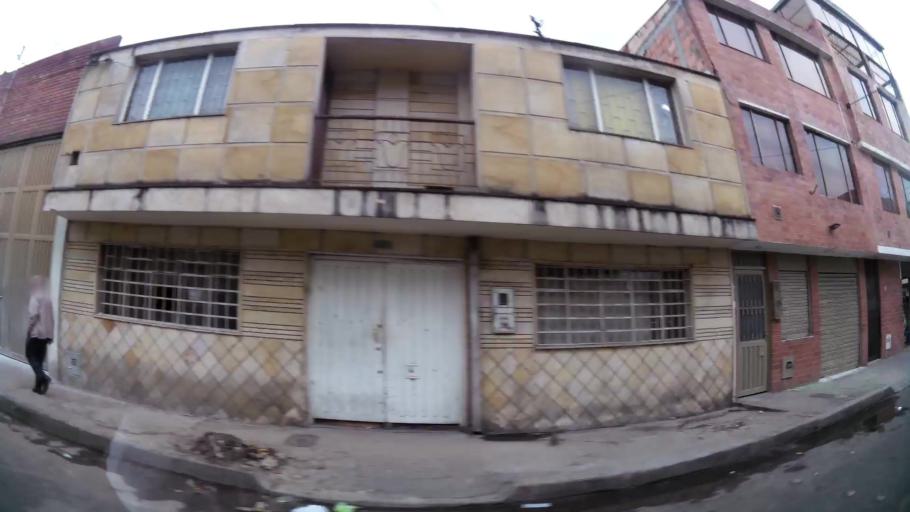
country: CO
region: Bogota D.C.
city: Bogota
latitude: 4.6771
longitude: -74.0982
